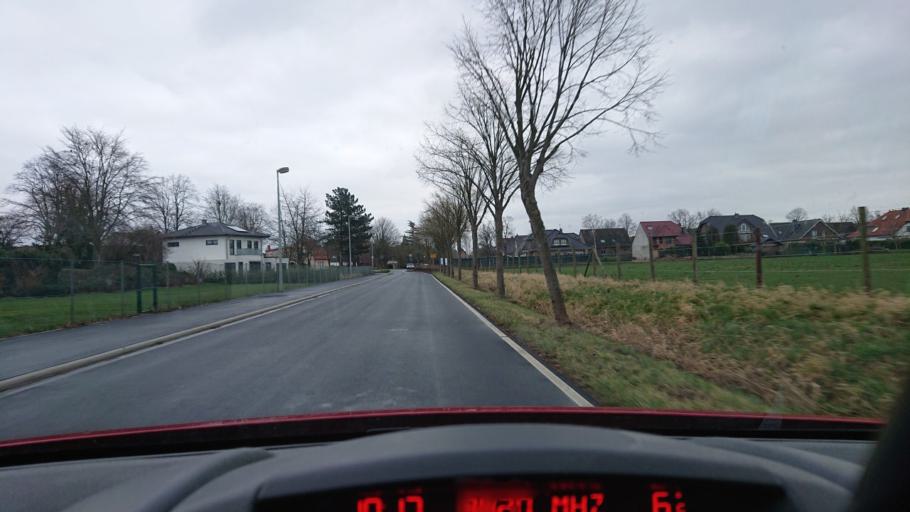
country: DE
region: North Rhine-Westphalia
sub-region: Regierungsbezirk Koln
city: Bergheim
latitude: 50.9130
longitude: 6.6292
